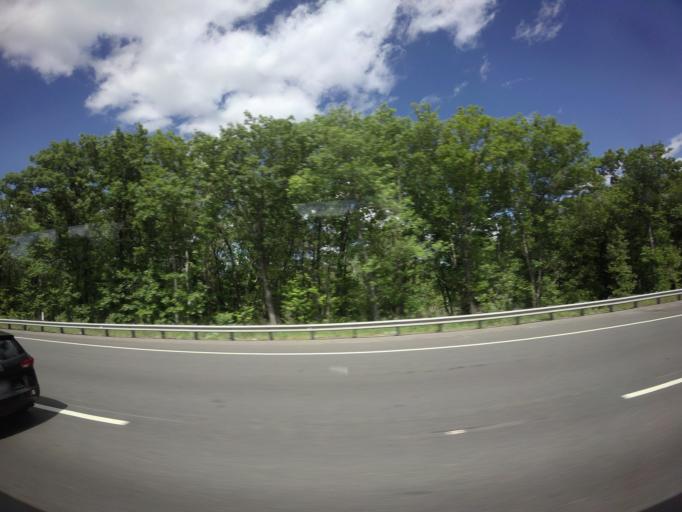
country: US
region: Massachusetts
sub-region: Middlesex County
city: Wilmington
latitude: 42.5543
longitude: -71.1383
